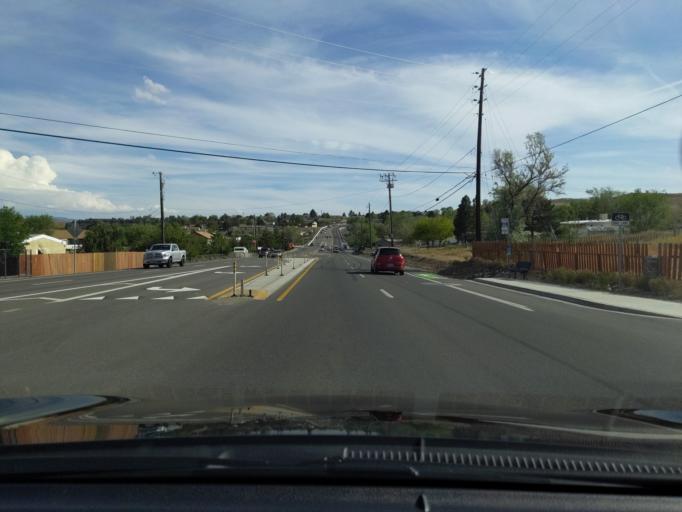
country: US
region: Nevada
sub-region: Washoe County
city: Sun Valley
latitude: 39.5735
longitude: -119.7814
